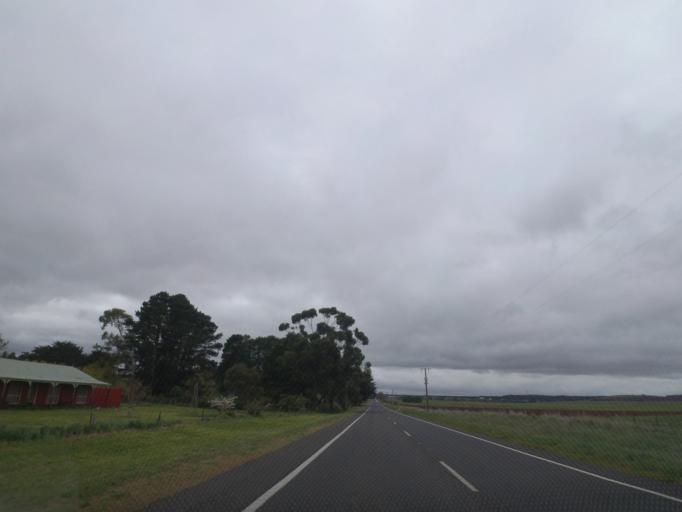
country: AU
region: Victoria
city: Brown Hill
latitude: -37.3817
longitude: 144.0130
